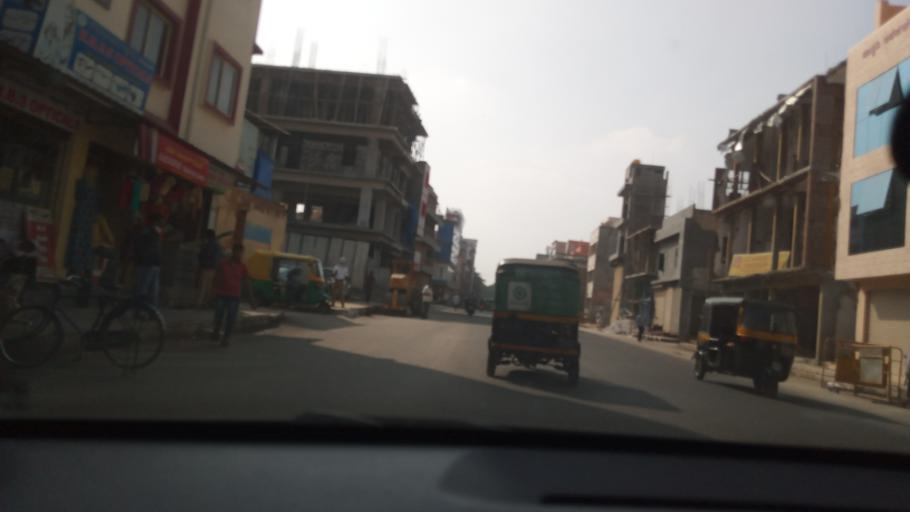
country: IN
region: Karnataka
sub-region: Mysore
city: Mysore
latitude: 12.3143
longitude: 76.6550
